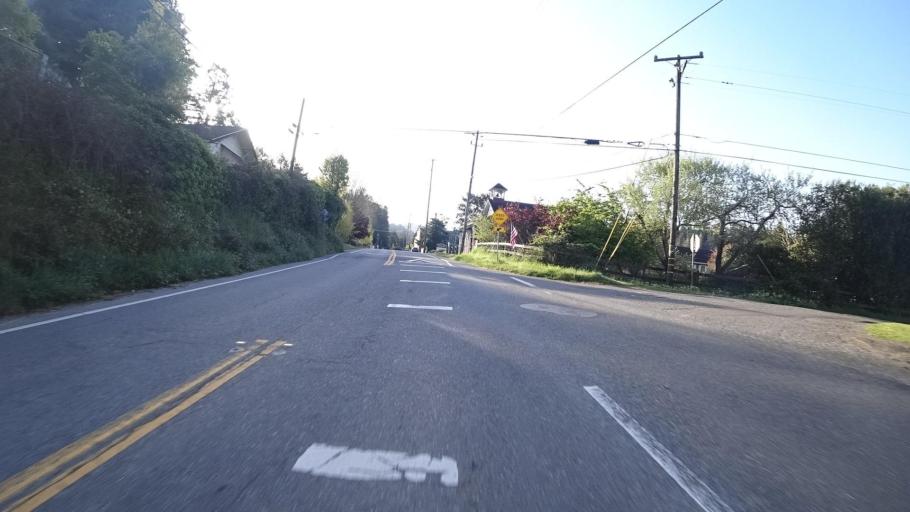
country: US
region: California
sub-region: Humboldt County
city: Myrtletown
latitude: 40.7618
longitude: -124.0620
